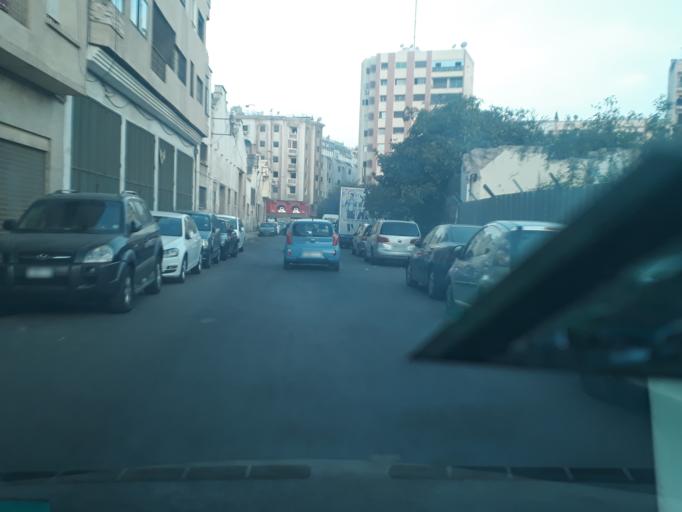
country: MA
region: Grand Casablanca
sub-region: Casablanca
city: Casablanca
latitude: 33.5748
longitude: -7.6404
